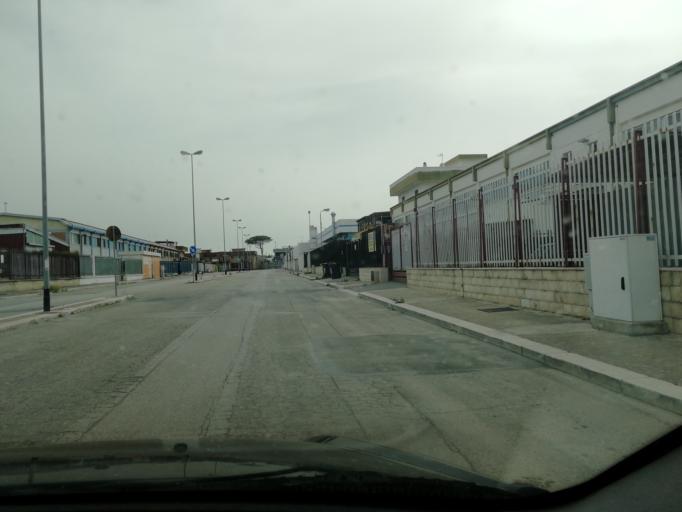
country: IT
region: Apulia
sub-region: Provincia di Barletta - Andria - Trani
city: Barletta
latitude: 41.3120
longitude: 16.3107
